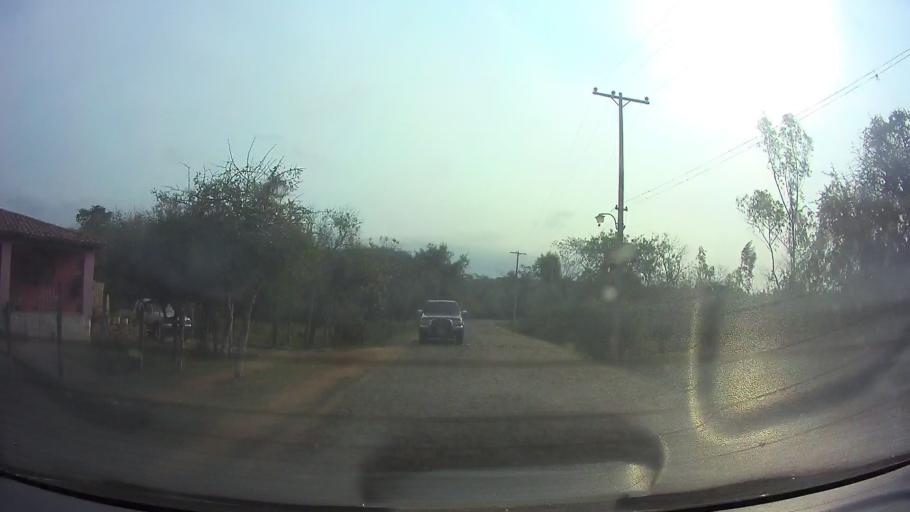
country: PY
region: Cordillera
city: Arroyos y Esteros
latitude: -25.0217
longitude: -57.1168
